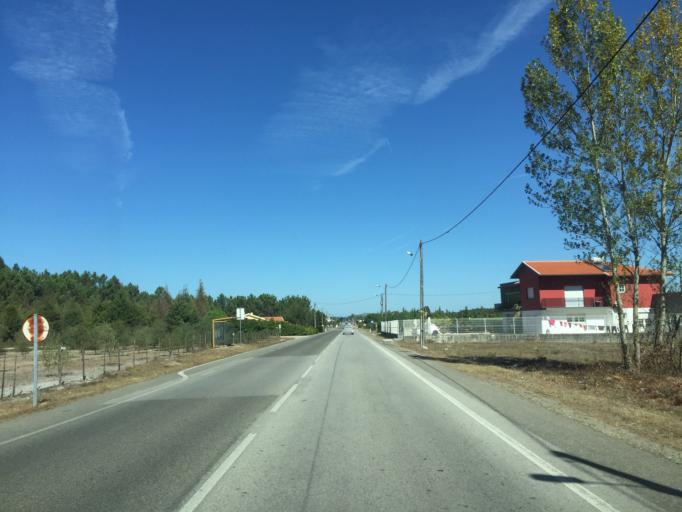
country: PT
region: Coimbra
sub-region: Figueira da Foz
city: Alhadas
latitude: 40.2251
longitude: -8.8043
